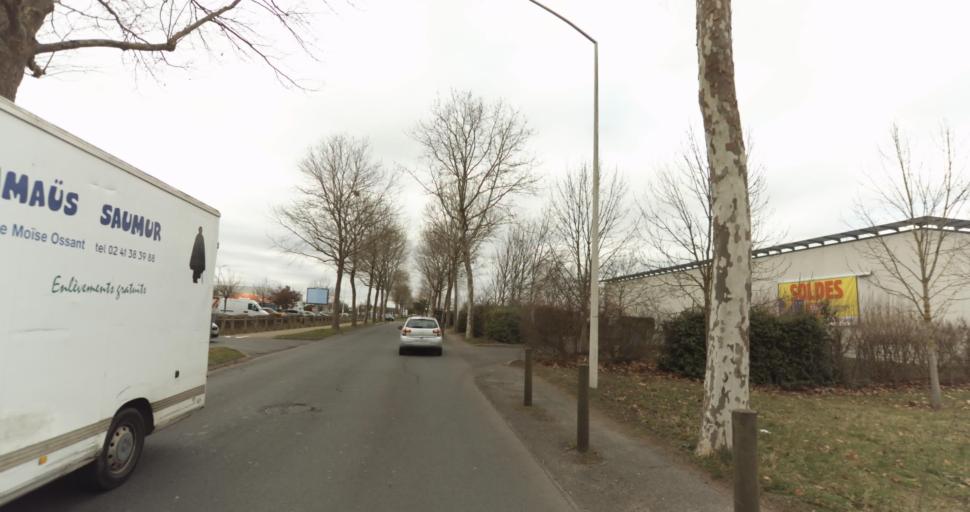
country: FR
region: Pays de la Loire
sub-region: Departement de Maine-et-Loire
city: Saumur
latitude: 47.2779
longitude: -0.0641
